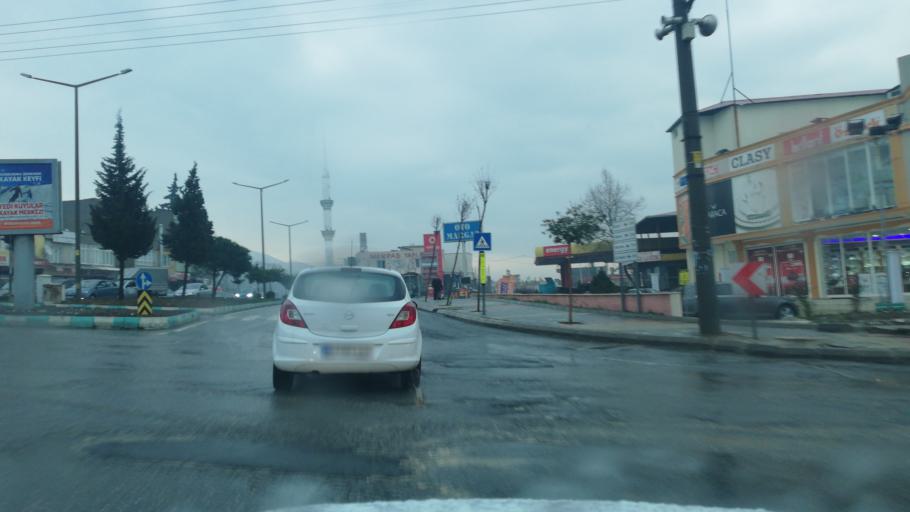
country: TR
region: Kahramanmaras
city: Kahramanmaras
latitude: 37.5817
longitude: 36.9457
